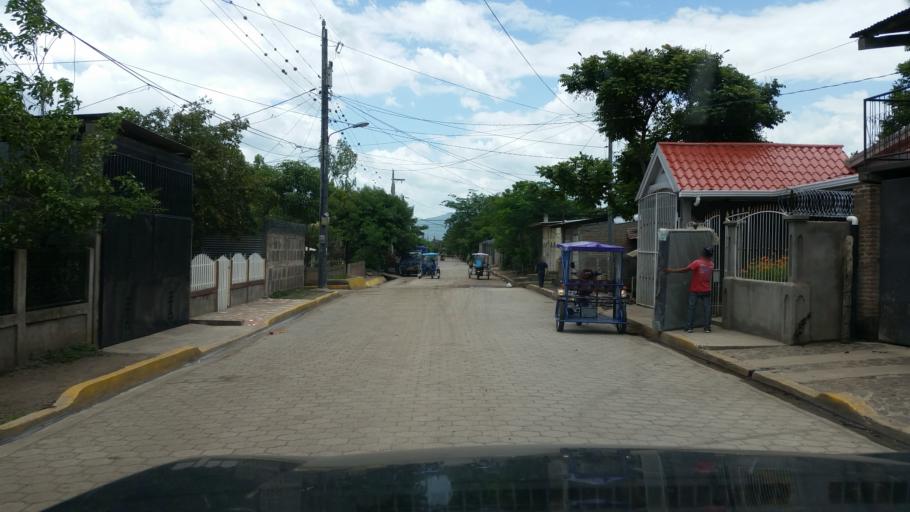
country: NI
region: Matagalpa
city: Ciudad Dario
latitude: 12.8569
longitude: -86.0921
